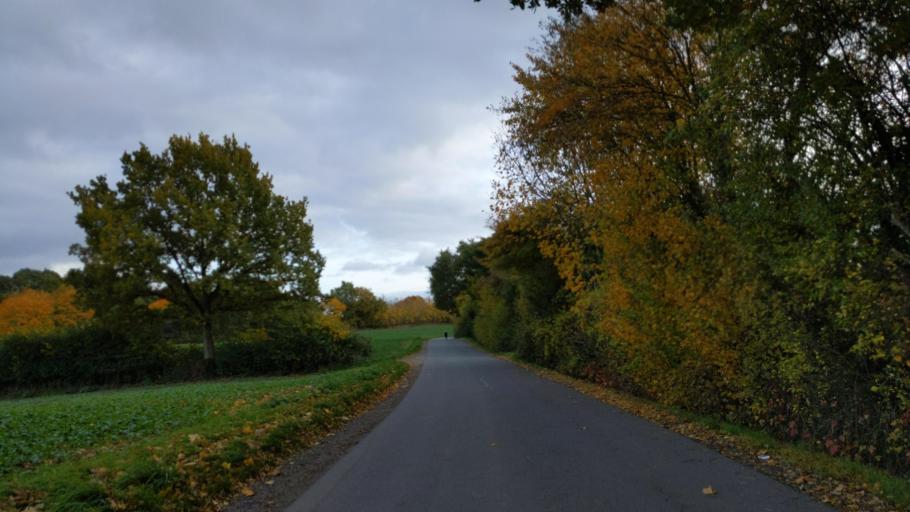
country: DE
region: Schleswig-Holstein
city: Sierksdorf
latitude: 54.0965
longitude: 10.7730
